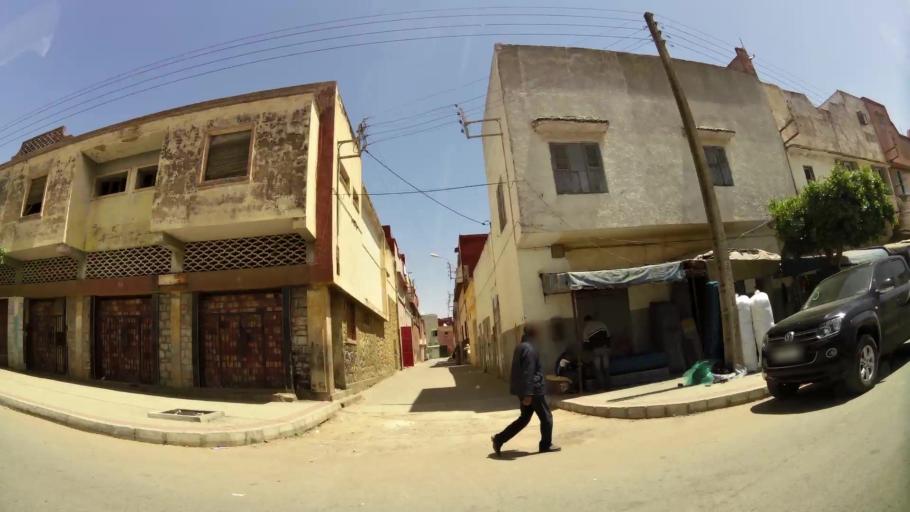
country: MA
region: Rabat-Sale-Zemmour-Zaer
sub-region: Khemisset
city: Khemisset
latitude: 33.8310
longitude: -6.0738
